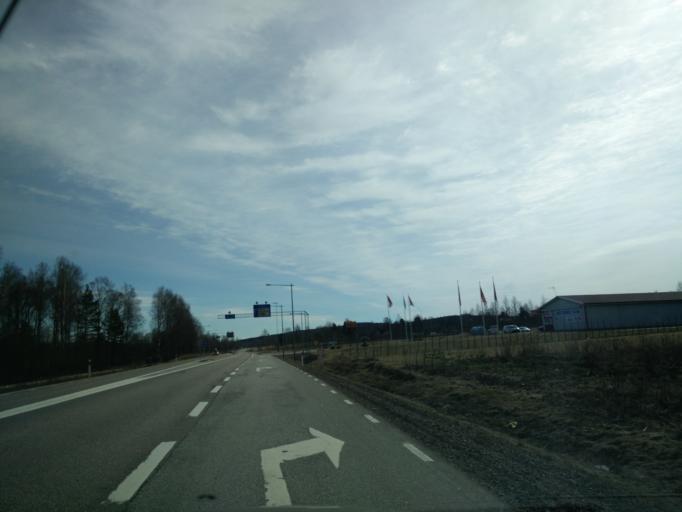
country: SE
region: Vaermland
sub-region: Hagfors Kommun
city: Hagfors
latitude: 60.0109
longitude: 13.5999
